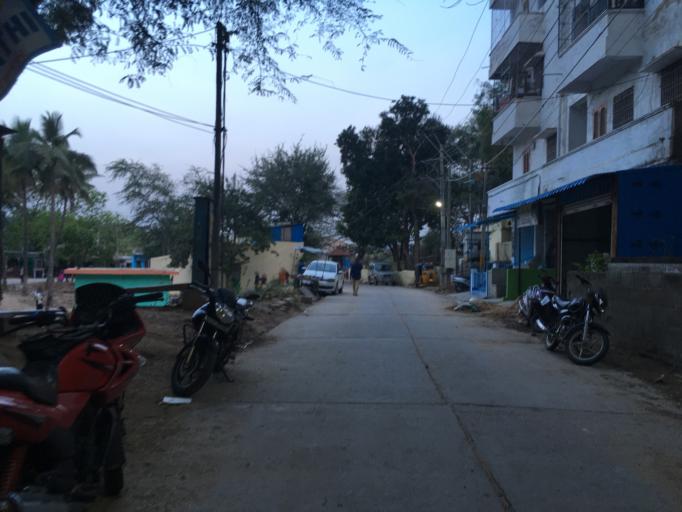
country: IN
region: Andhra Pradesh
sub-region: Anantapur
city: Puttaparthi
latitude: 14.1643
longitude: 77.8146
